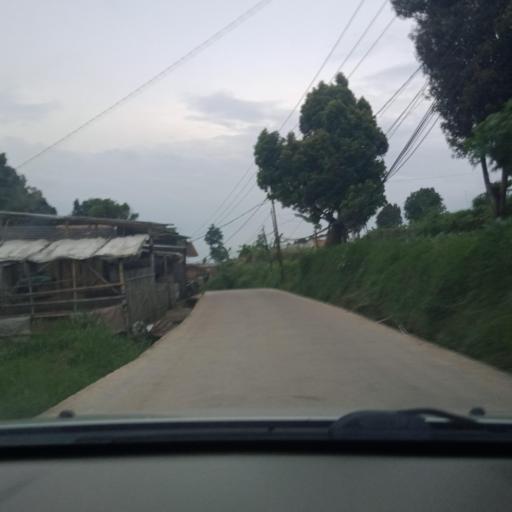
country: ID
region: West Java
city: Lembang
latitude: -6.8392
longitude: 107.5849
